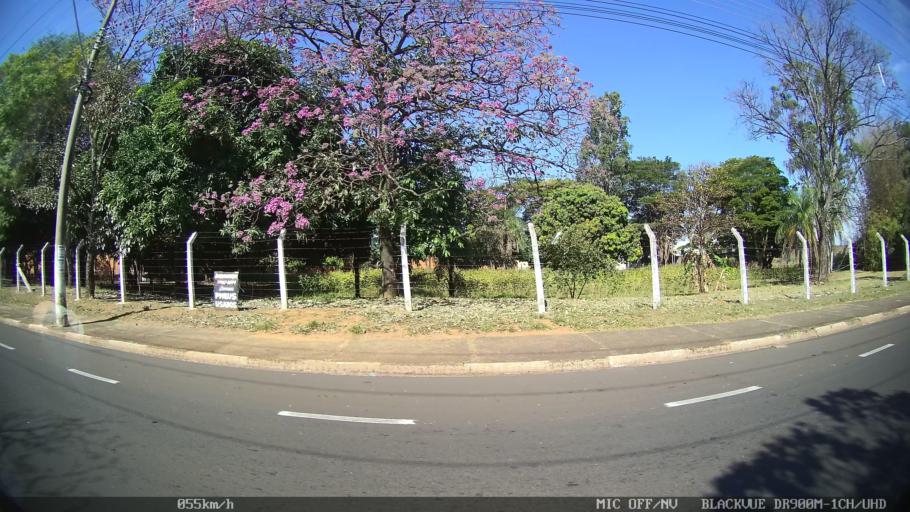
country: BR
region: Sao Paulo
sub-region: Franca
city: Franca
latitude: -20.5443
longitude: -47.4252
